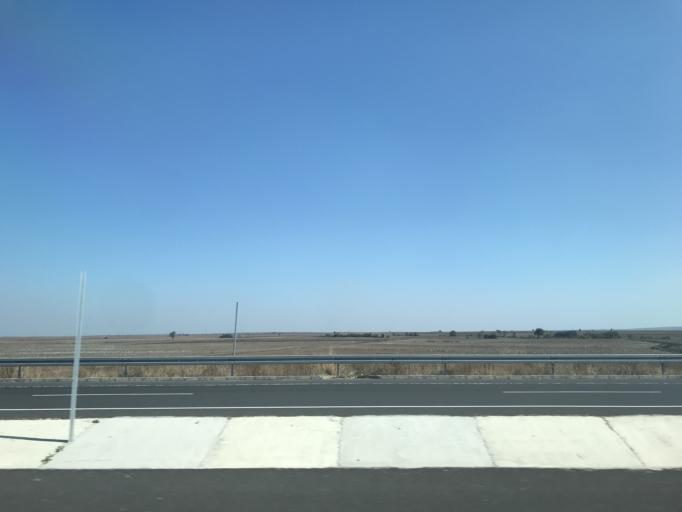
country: TR
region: Tekirdag
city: Muratli
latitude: 41.1859
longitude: 27.5394
